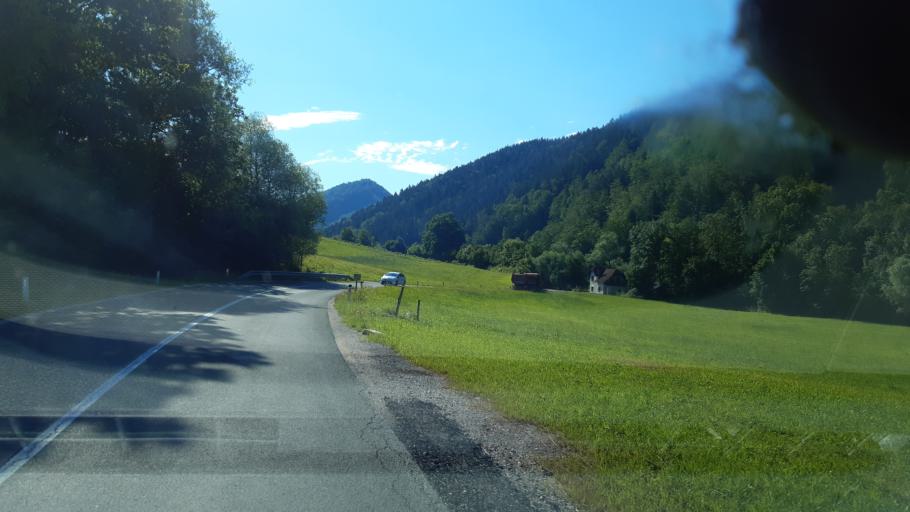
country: SI
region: Lukovica
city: Lukovica pri Domzalah
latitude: 46.2181
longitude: 14.7111
